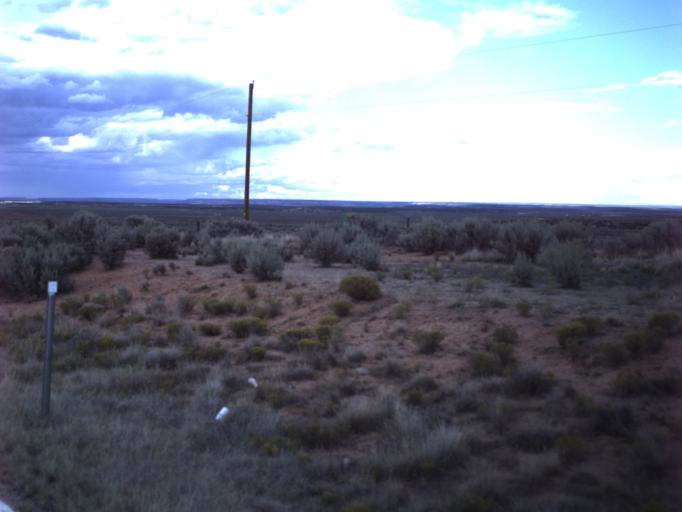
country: US
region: Utah
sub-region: San Juan County
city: Blanding
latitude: 37.3946
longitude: -109.3386
